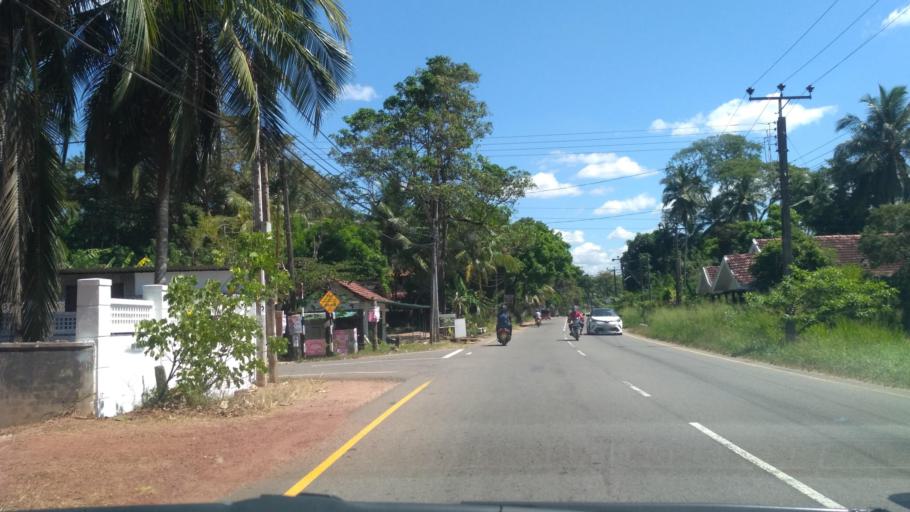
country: LK
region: North Western
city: Kuliyapitiya
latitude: 7.3235
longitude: 80.0953
